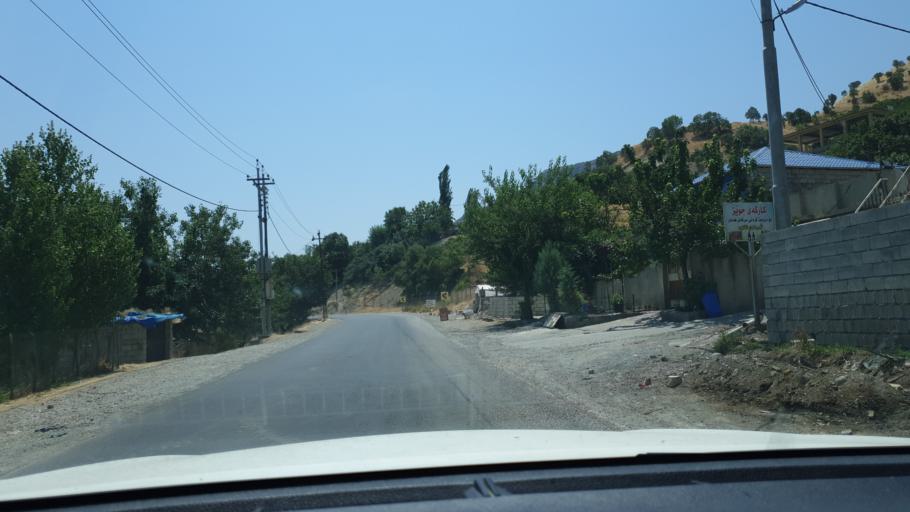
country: IQ
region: Arbil
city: Nahiyat Hiran
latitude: 36.2940
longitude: 44.4756
